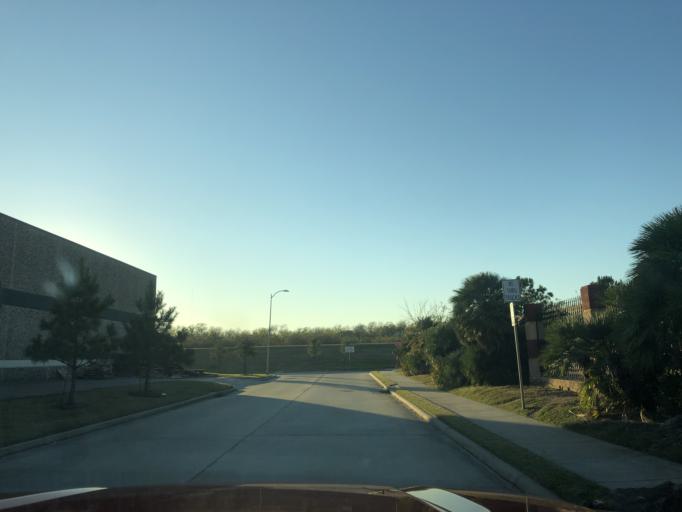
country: US
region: Texas
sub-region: Harris County
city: Jacinto City
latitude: 29.7585
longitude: -95.2678
